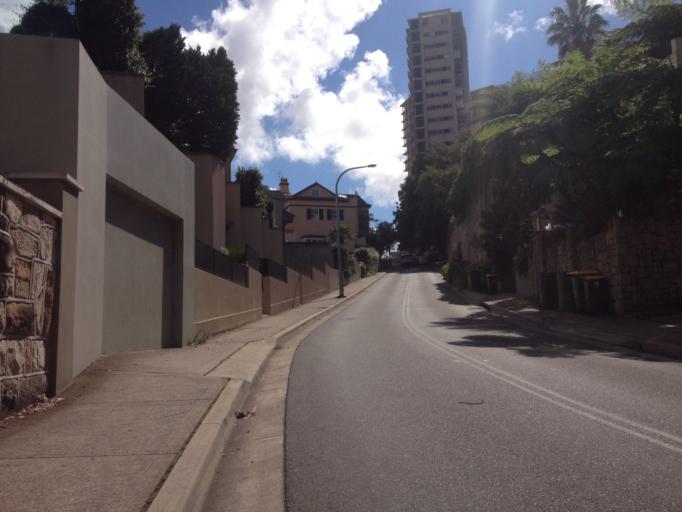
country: AU
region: New South Wales
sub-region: Woollahra
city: Darling Point
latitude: -33.8704
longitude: 151.2363
